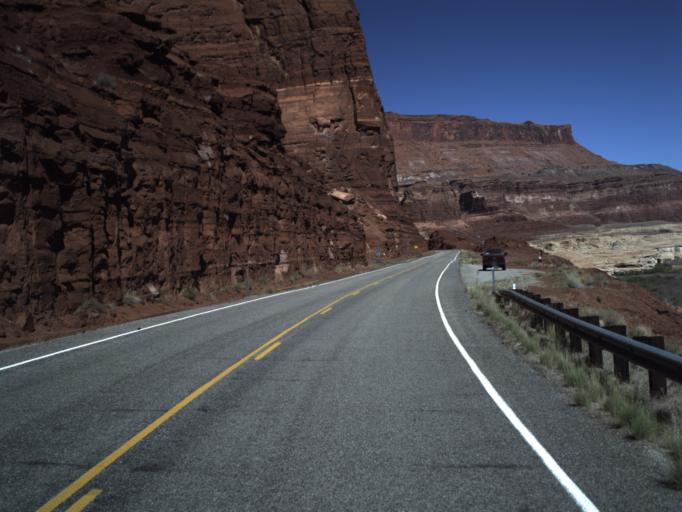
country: US
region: Utah
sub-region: San Juan County
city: Blanding
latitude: 37.8945
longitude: -110.3977
